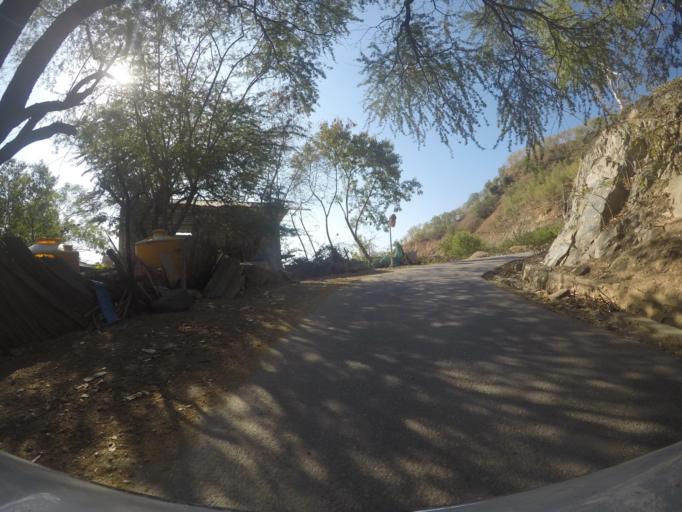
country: TL
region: Dili
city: Dili
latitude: -8.5379
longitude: 125.6165
